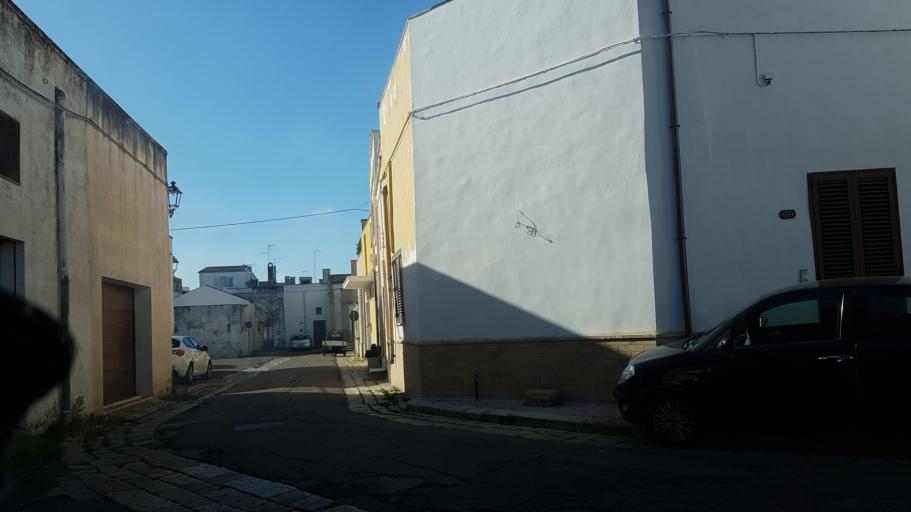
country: IT
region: Apulia
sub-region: Provincia di Lecce
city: Campi Salentina
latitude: 40.3976
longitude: 18.0218
